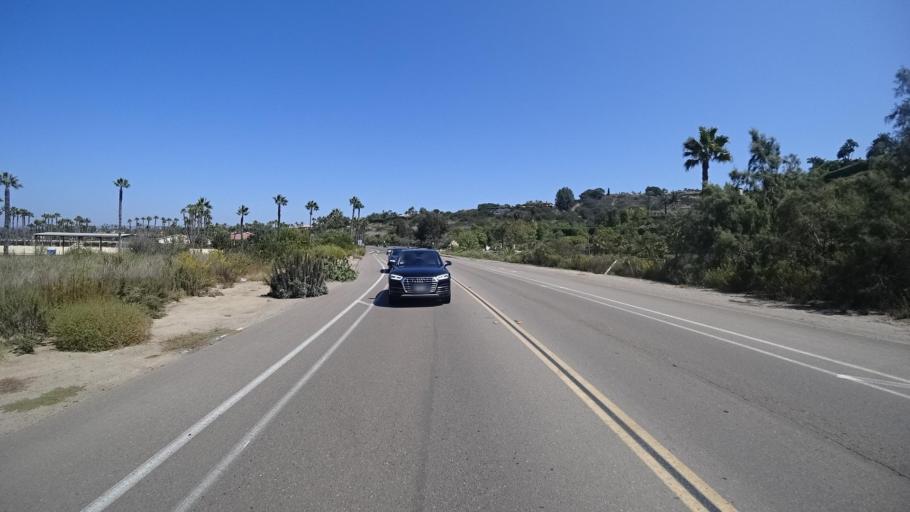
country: US
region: California
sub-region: San Diego County
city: Fairbanks Ranch
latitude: 32.9843
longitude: -117.1977
